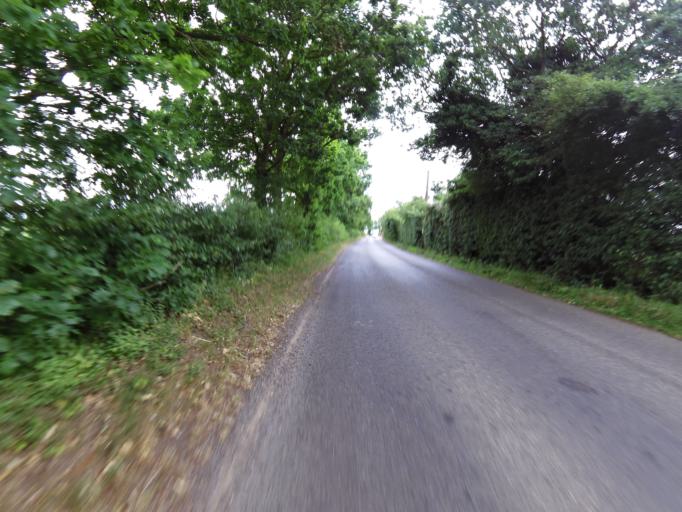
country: GB
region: England
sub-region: Norfolk
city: Harleston
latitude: 52.4030
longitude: 1.2780
